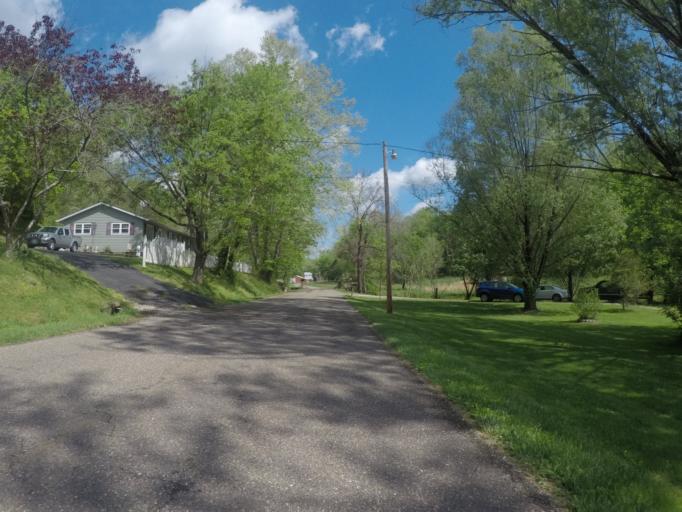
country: US
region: West Virginia
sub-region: Cabell County
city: Huntington
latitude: 38.5231
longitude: -82.4405
